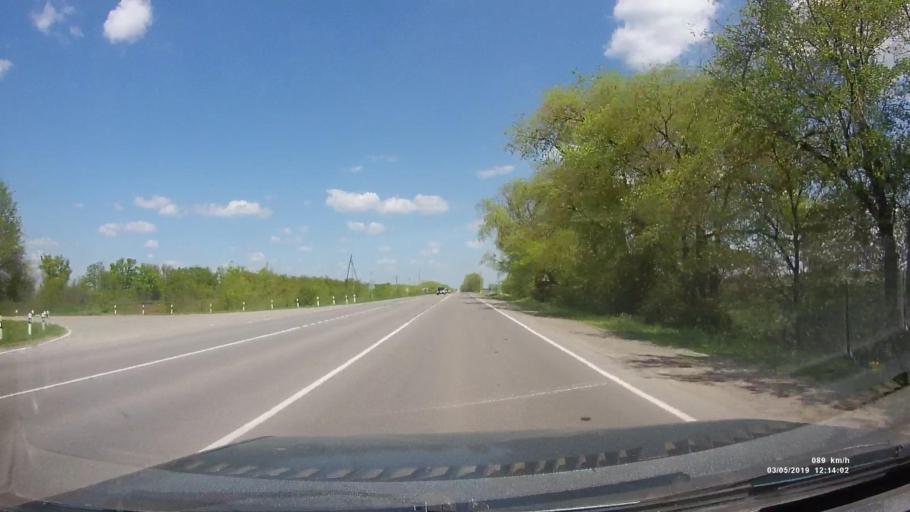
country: RU
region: Rostov
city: Melikhovskaya
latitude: 47.3387
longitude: 40.5594
